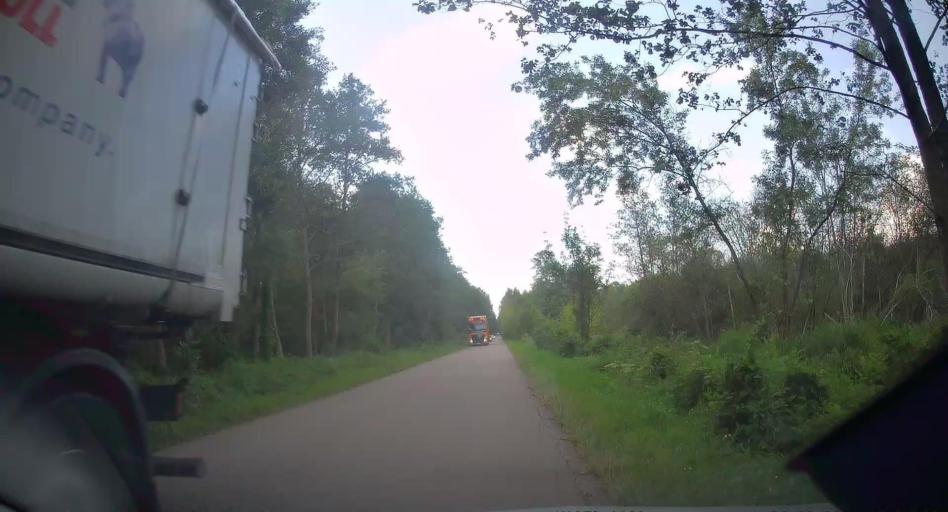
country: PL
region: Swietokrzyskie
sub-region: Powiat konecki
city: Ruda Maleniecka
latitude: 51.1376
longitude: 20.2428
